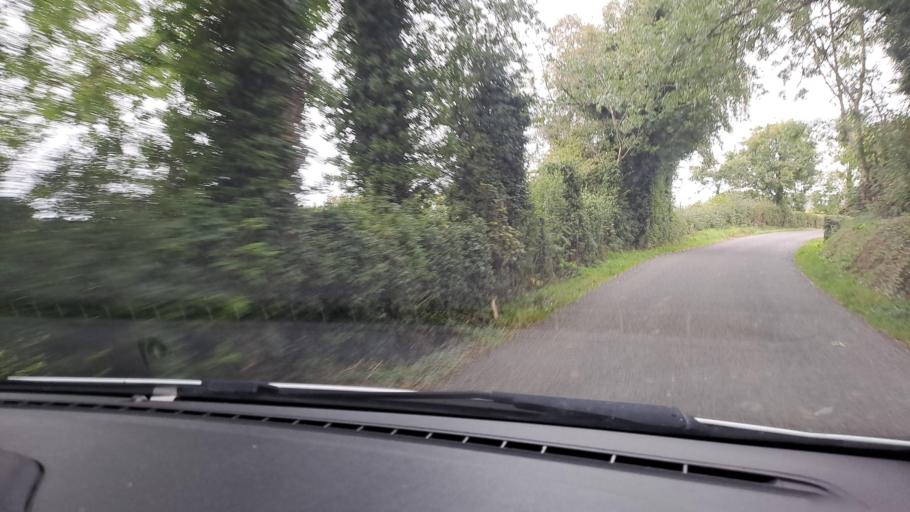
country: IE
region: Ulster
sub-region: County Monaghan
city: Castleblayney
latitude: 54.0371
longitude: -6.8108
